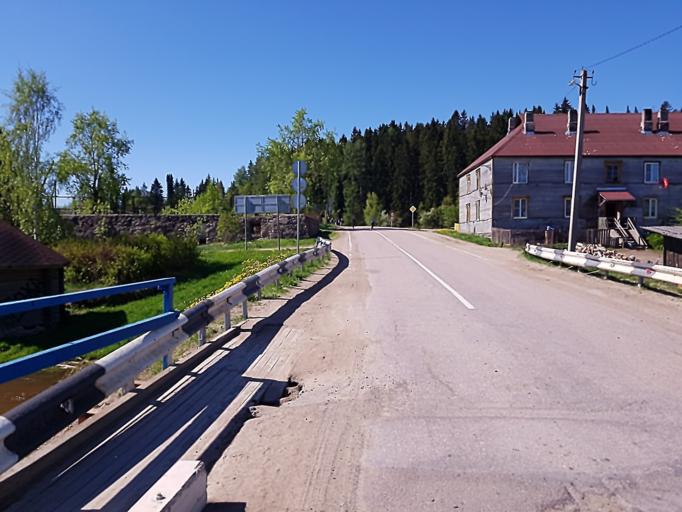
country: RU
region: Leningrad
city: Kuznechnoye
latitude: 61.2989
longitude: 29.8880
